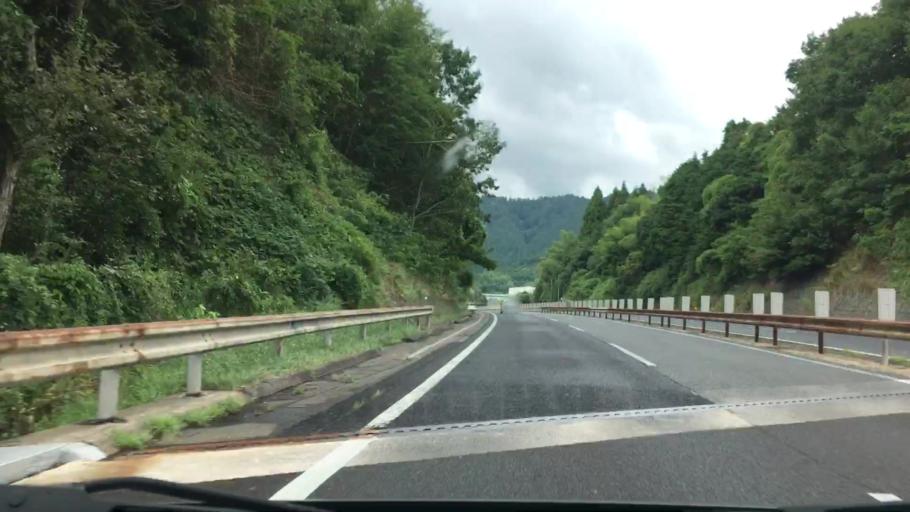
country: JP
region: Okayama
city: Tsuyama
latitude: 35.0236
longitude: 133.7379
